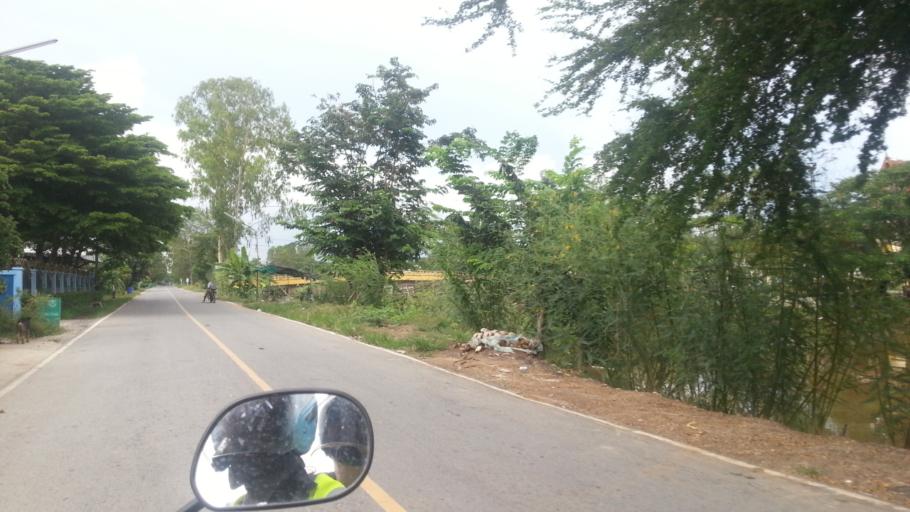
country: TH
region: Pathum Thani
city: Nong Suea
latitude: 14.1957
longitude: 100.8230
